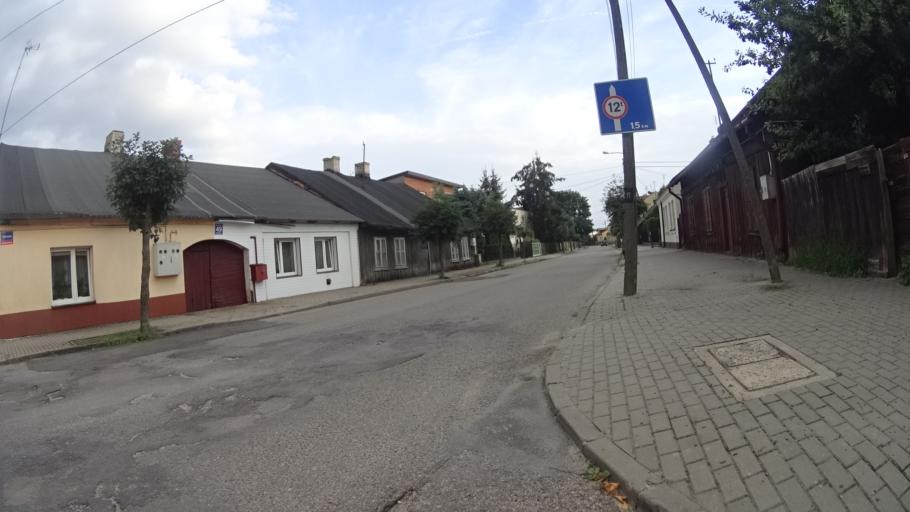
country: PL
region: Masovian Voivodeship
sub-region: Powiat grojecki
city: Mogielnica
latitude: 51.6918
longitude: 20.7258
